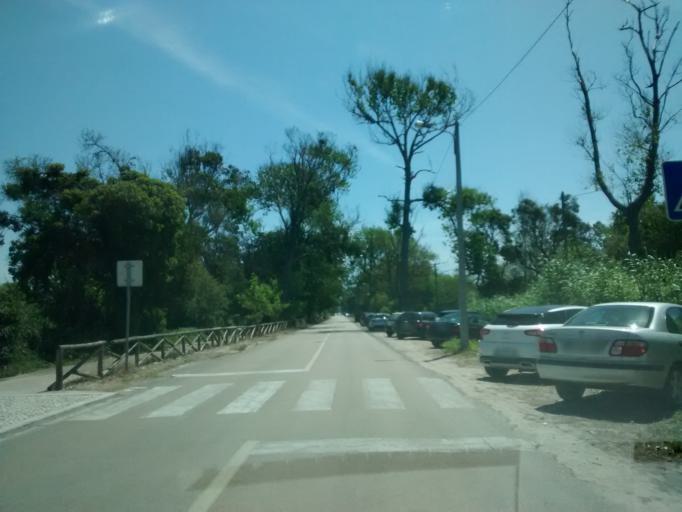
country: PT
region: Coimbra
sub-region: Mira
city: Mira
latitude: 40.4473
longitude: -8.8000
